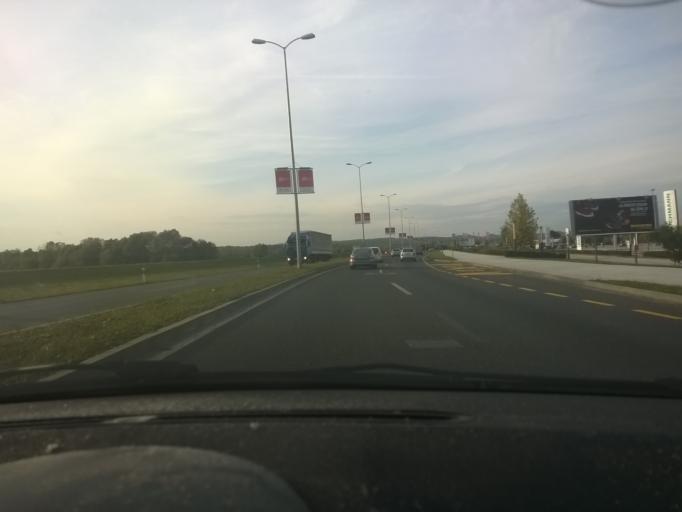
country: HR
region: Zagrebacka
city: Zapresic
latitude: 45.8693
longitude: 15.8241
